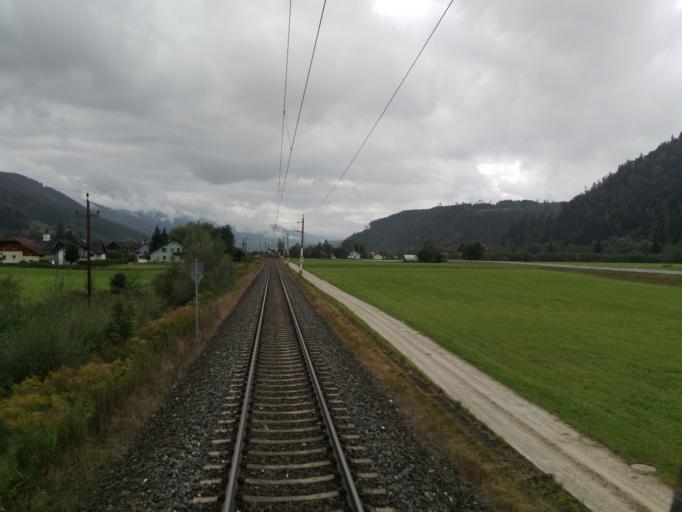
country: AT
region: Styria
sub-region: Politischer Bezirk Liezen
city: Oblarn
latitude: 47.4653
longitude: 13.9972
